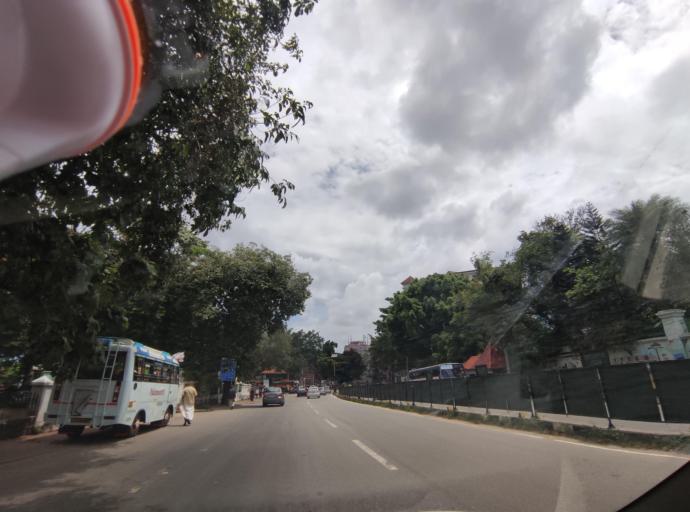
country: IN
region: Kerala
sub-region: Thiruvananthapuram
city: Thiruvananthapuram
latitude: 8.5086
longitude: 76.9497
